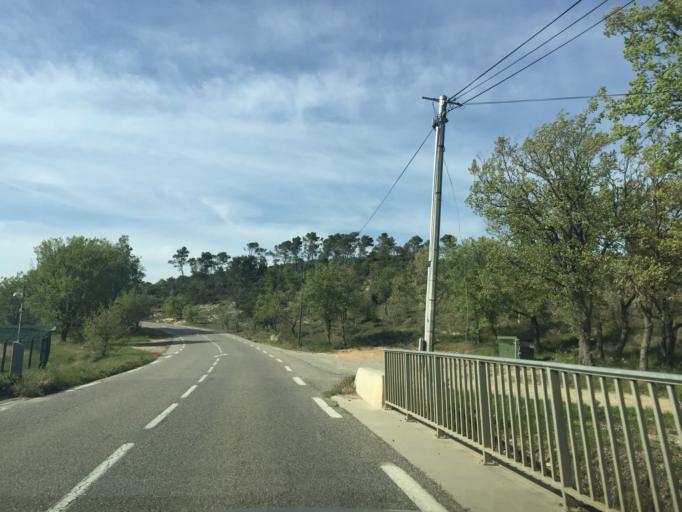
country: FR
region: Provence-Alpes-Cote d'Azur
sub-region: Departement du Var
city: Ginasservis
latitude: 43.6929
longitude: 5.8360
